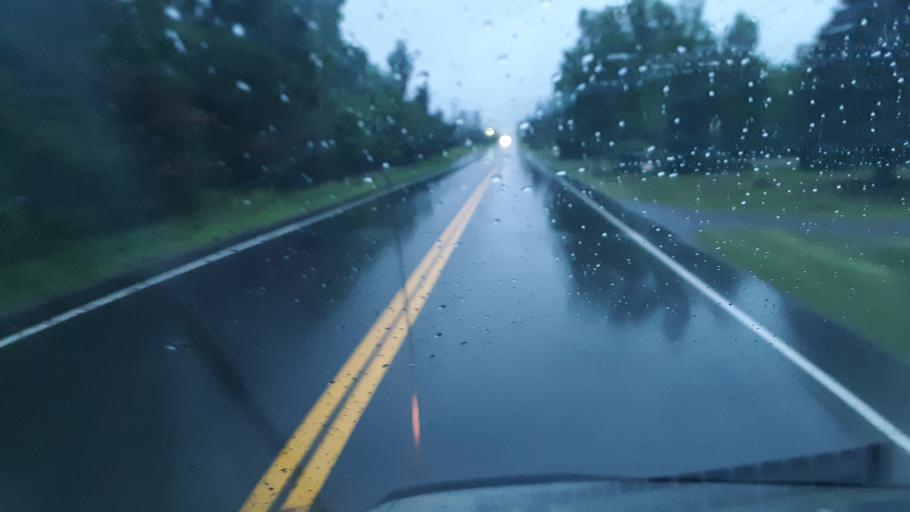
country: US
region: Maine
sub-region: Penobscot County
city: Patten
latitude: 45.9604
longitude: -68.4518
